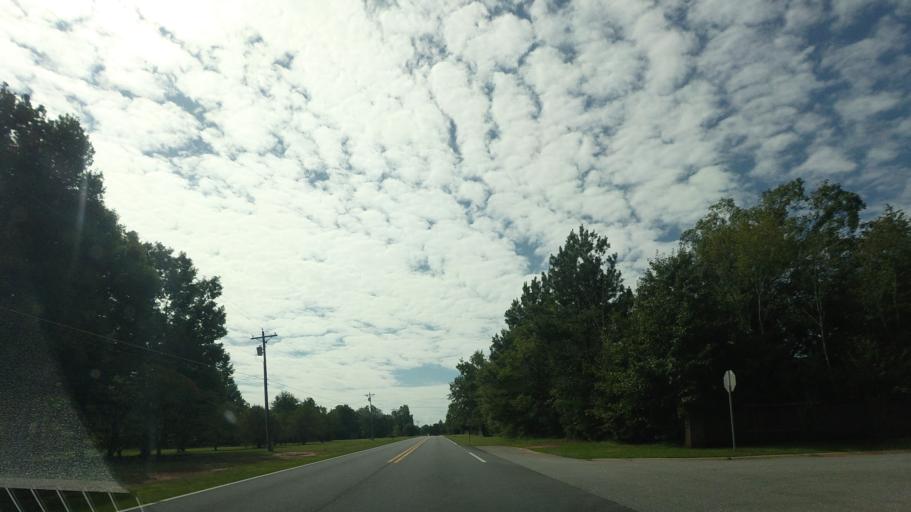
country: US
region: Georgia
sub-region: Houston County
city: Centerville
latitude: 32.6521
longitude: -83.6959
